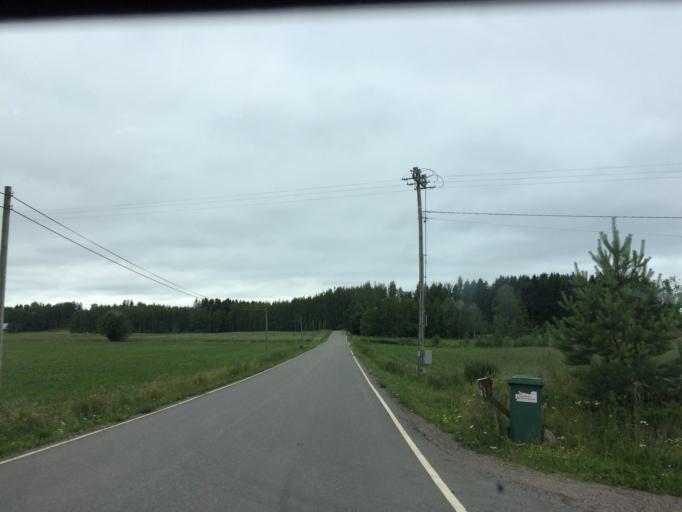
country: FI
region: Haeme
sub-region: Haemeenlinna
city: Janakkala
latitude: 60.8493
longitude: 24.5263
